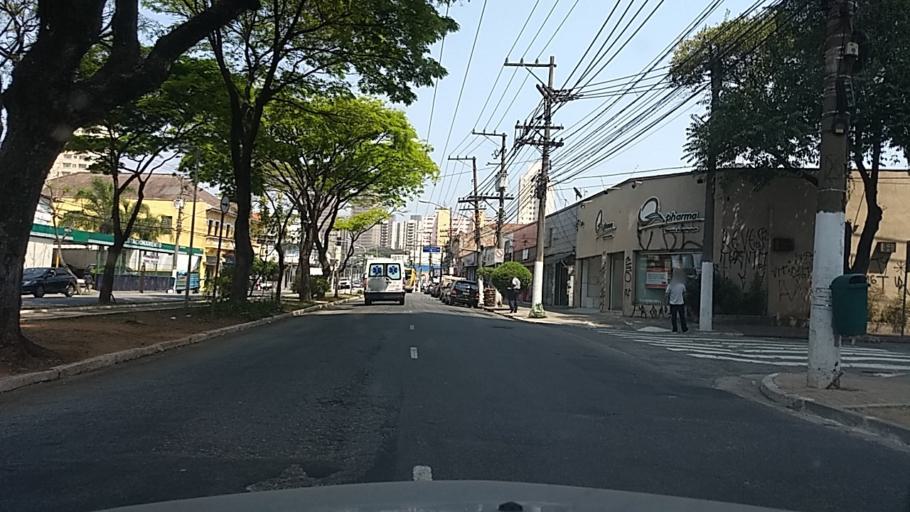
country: BR
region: Sao Paulo
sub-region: Sao Paulo
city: Sao Paulo
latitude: -23.5341
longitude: -46.5676
